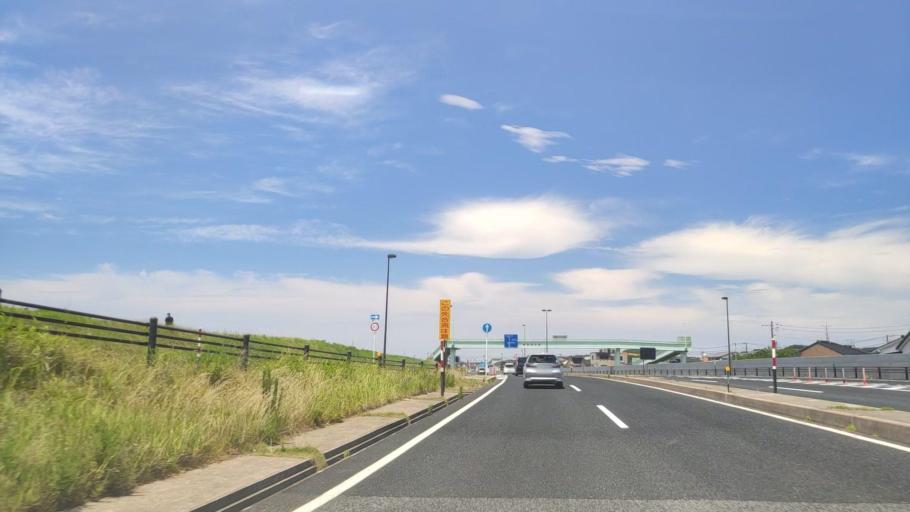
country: JP
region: Tottori
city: Tottori
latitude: 35.5004
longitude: 134.2181
